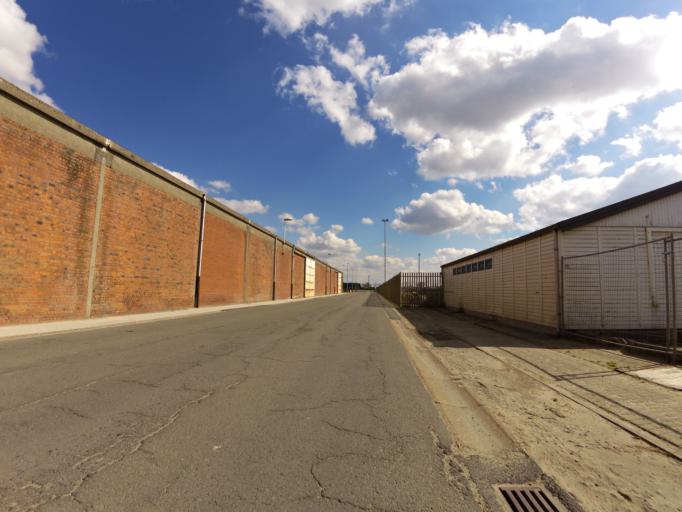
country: BE
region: Flanders
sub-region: Provincie West-Vlaanderen
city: Ostend
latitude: 51.2214
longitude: 2.9352
